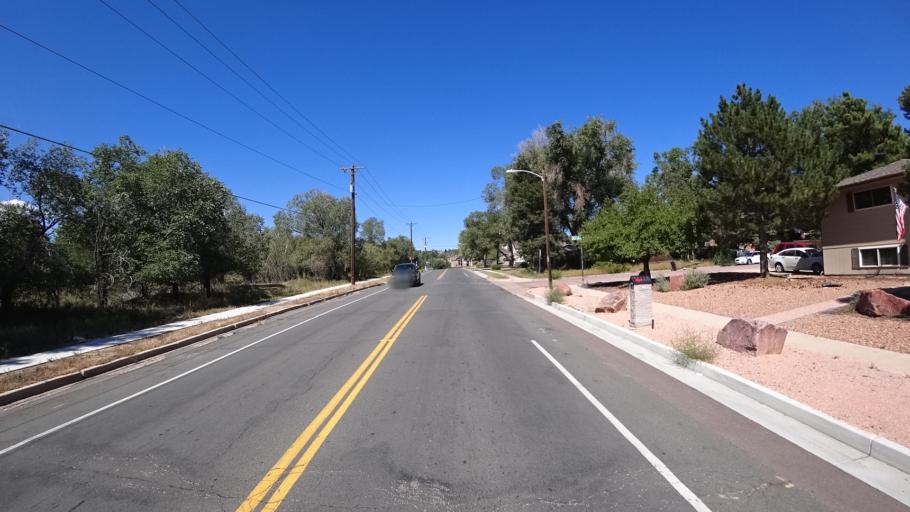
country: US
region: Colorado
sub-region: El Paso County
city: Colorado Springs
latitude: 38.8547
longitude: -104.8497
